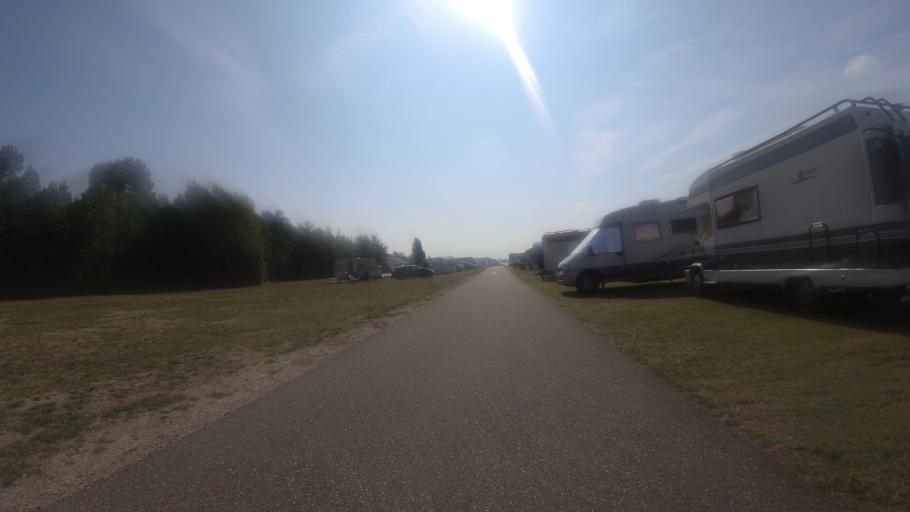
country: NL
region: Zeeland
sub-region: Gemeente Veere
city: Veere
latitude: 51.5698
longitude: 3.6546
